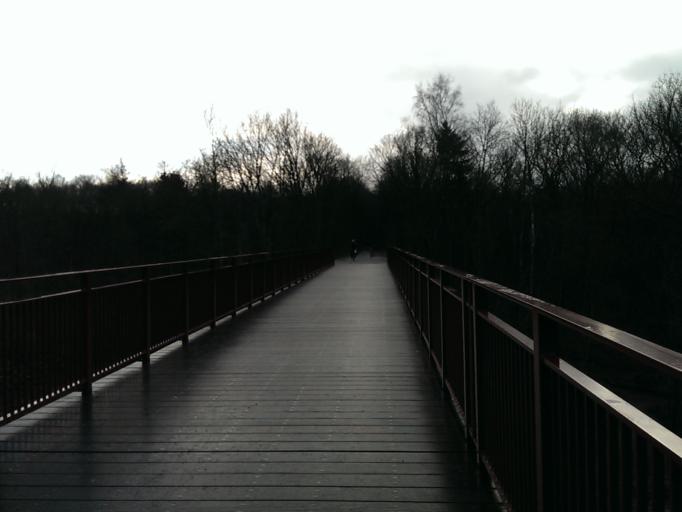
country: DK
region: Central Jutland
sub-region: Horsens Kommune
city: Braedstrup
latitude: 55.9730
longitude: 9.6896
